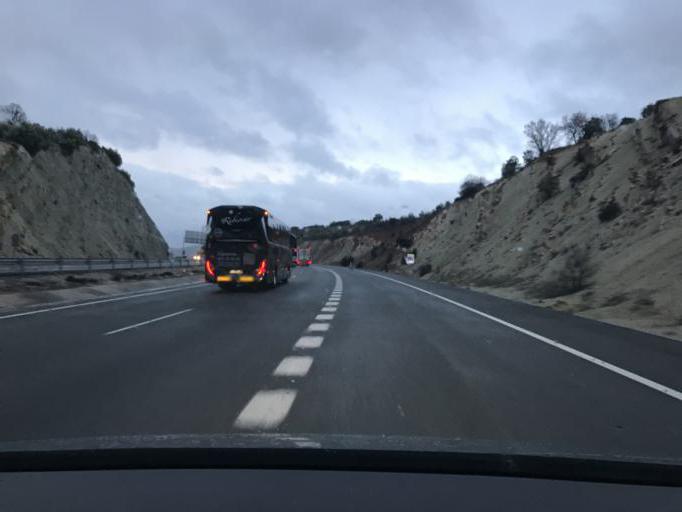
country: ES
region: Andalusia
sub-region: Provincia de Granada
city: Campotejar
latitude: 37.4683
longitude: -3.5701
